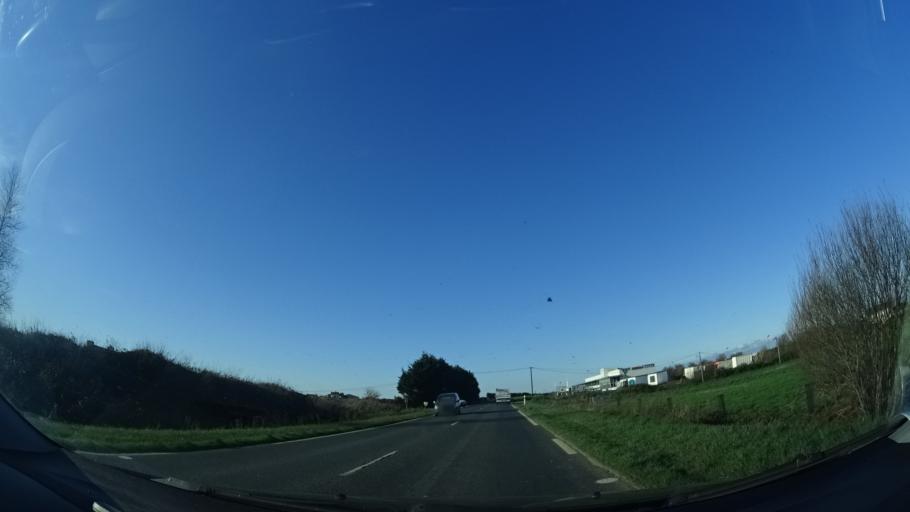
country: FR
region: Brittany
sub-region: Departement du Finistere
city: Saint-Pol-de-Leon
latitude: 48.6647
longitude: -3.9947
